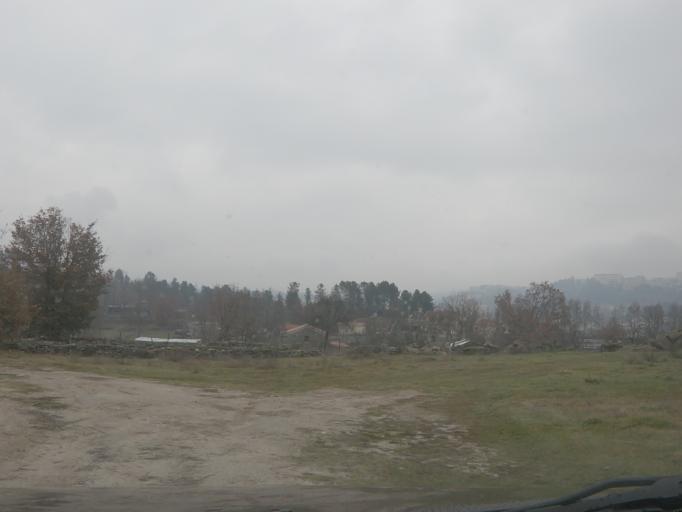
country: PT
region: Vila Real
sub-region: Vila Real
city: Vila Real
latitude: 41.2997
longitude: -7.7663
